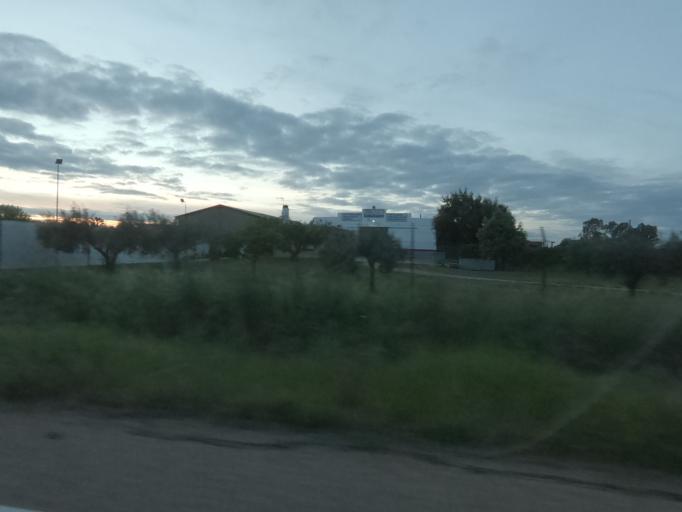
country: ES
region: Extremadura
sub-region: Provincia de Badajoz
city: Badajoz
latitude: 38.9286
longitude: -6.9322
